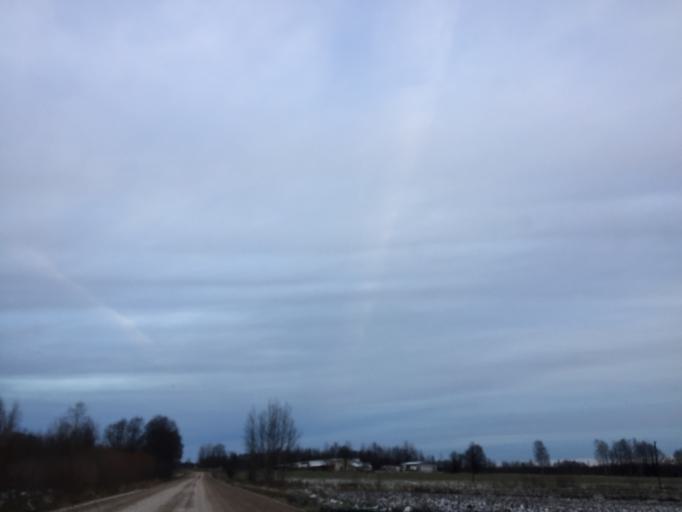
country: LV
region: Limbazu Rajons
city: Limbazi
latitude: 57.5894
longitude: 24.8441
